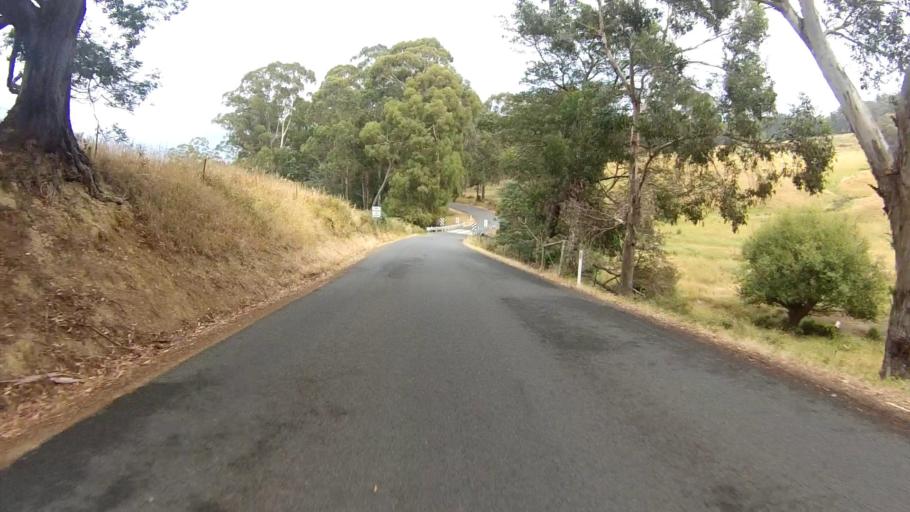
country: AU
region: Tasmania
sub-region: Huon Valley
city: Cygnet
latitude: -43.1808
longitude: 147.1149
